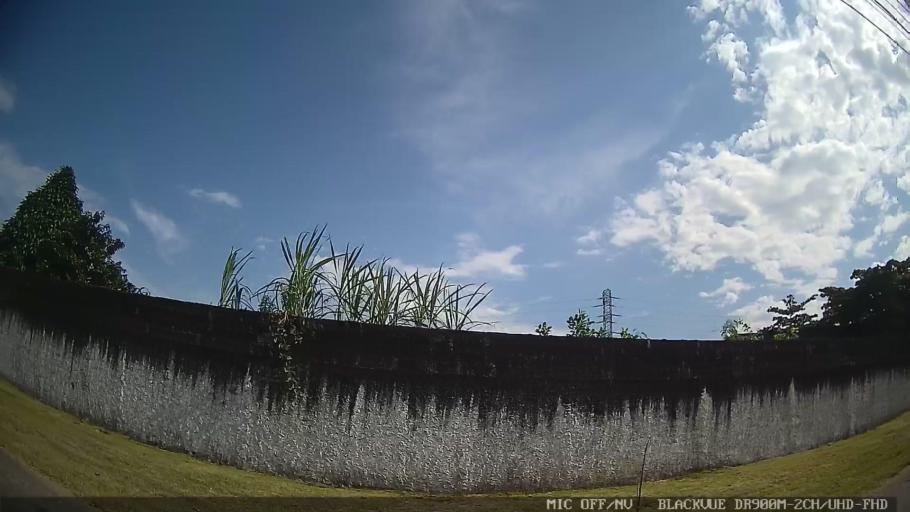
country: BR
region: Sao Paulo
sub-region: Guaruja
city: Guaruja
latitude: -23.9633
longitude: -46.2760
